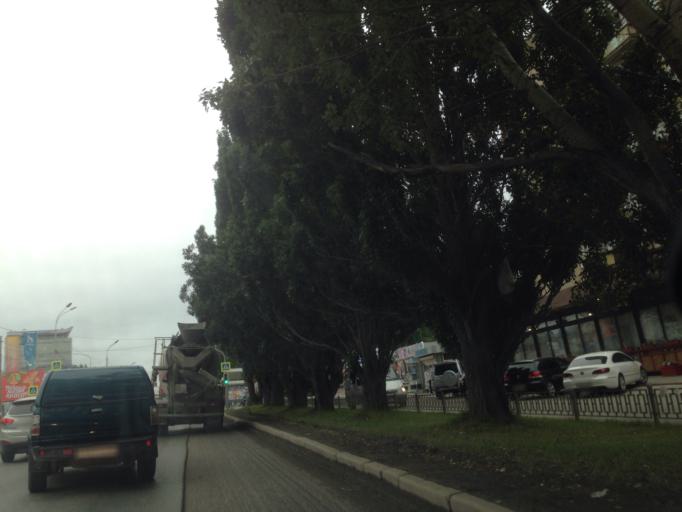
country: RU
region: Sverdlovsk
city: Yekaterinburg
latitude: 56.8360
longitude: 60.6339
